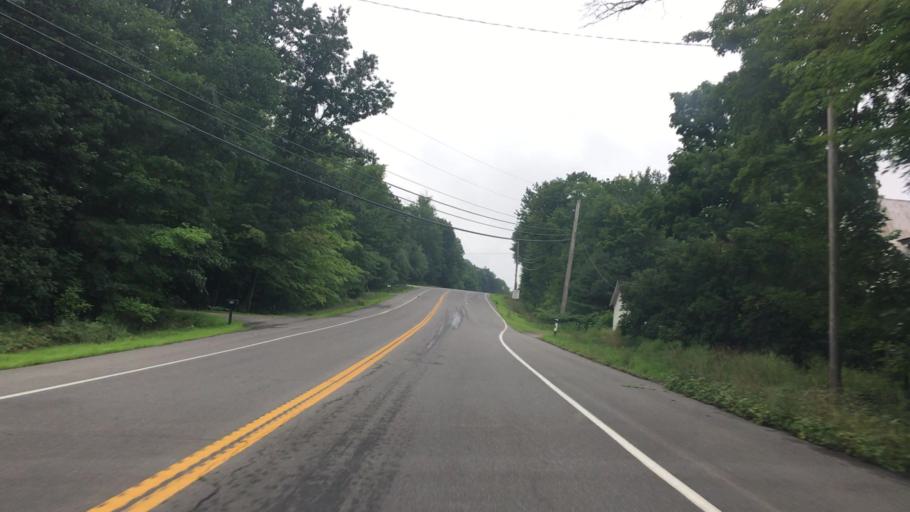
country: US
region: Maine
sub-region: York County
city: Sanford (historical)
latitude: 43.4273
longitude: -70.8110
